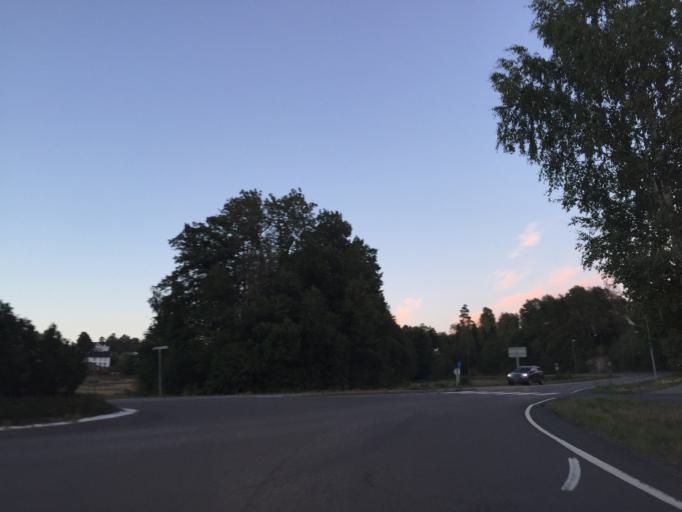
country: NO
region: Ostfold
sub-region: Moss
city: Moss
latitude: 59.5123
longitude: 10.6856
